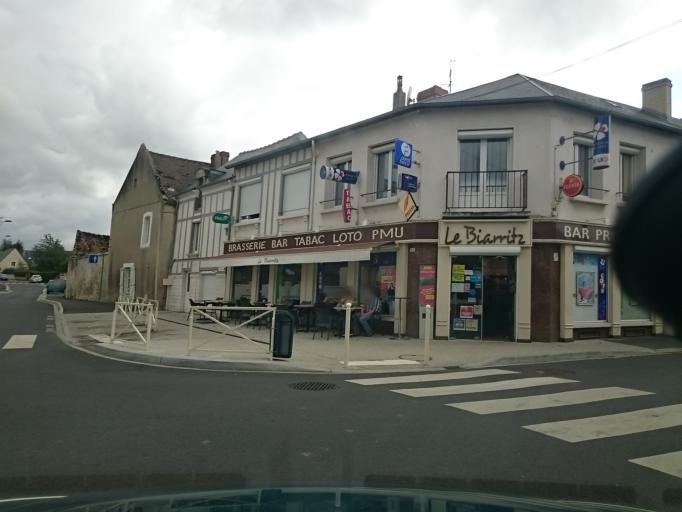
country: FR
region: Lower Normandy
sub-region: Departement du Calvados
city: Ifs
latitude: 49.1425
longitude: -0.3482
